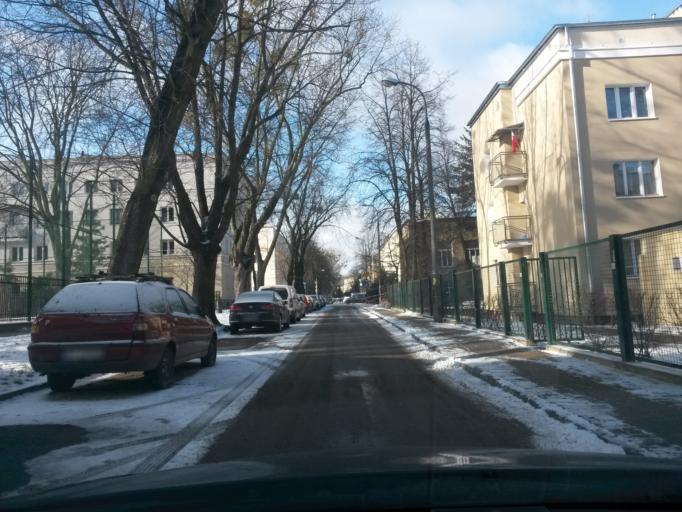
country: PL
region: Masovian Voivodeship
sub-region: Warszawa
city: Wola
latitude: 52.2463
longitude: 20.9490
